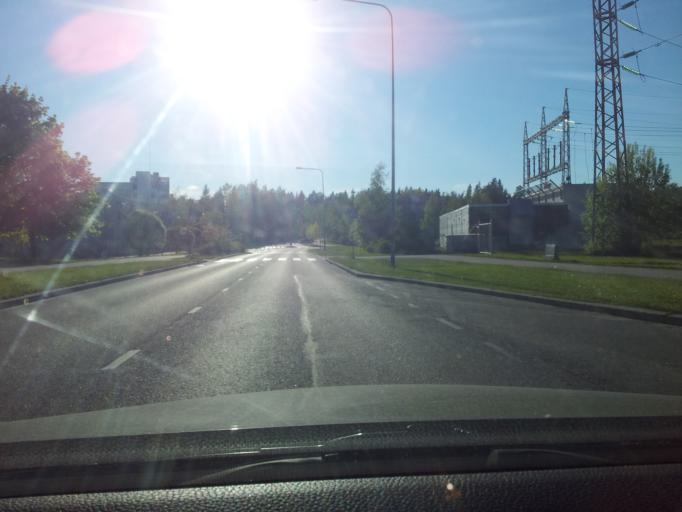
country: FI
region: Uusimaa
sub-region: Helsinki
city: Kilo
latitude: 60.2084
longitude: 24.7684
